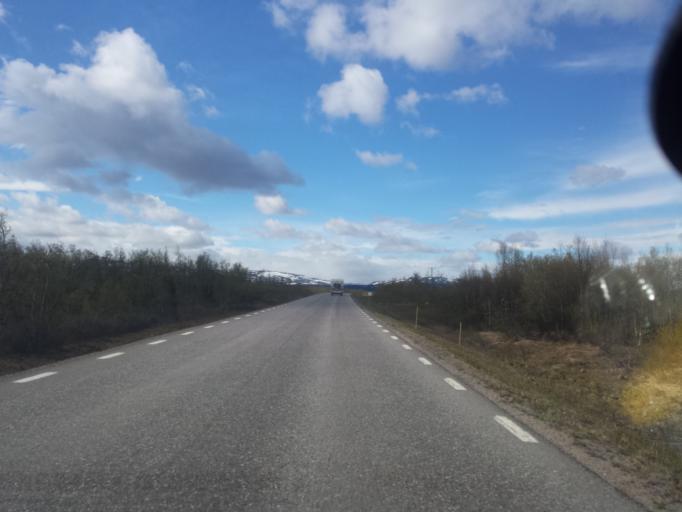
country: SE
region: Norrbotten
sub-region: Kiruna Kommun
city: Kiruna
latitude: 68.0015
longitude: 19.8590
